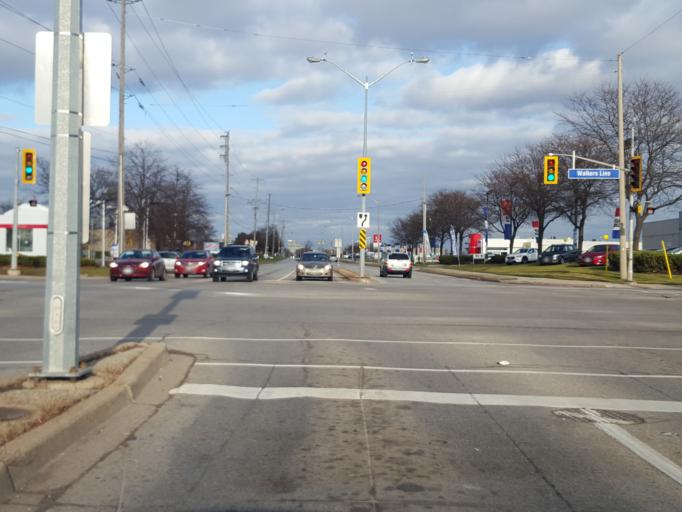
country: CA
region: Ontario
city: Burlington
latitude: 43.3627
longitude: -79.7836
